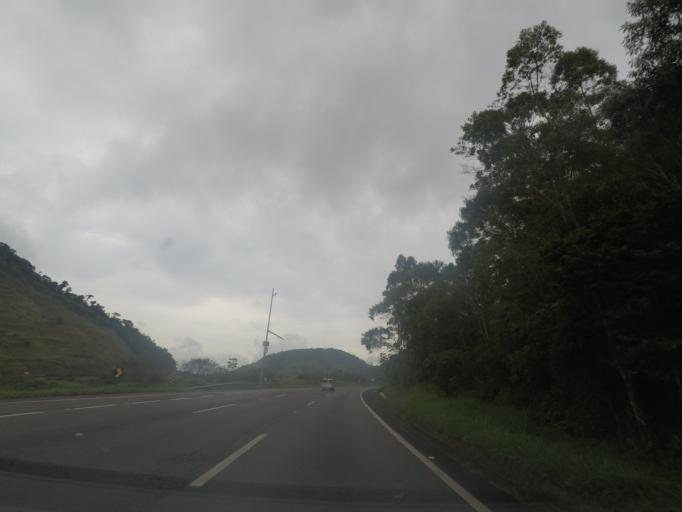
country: BR
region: Sao Paulo
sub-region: Cajati
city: Cajati
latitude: -24.8930
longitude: -48.2398
